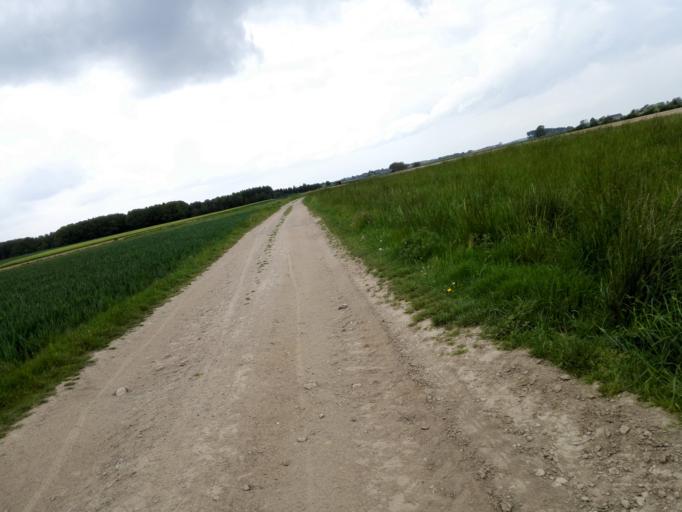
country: BE
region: Flanders
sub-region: Provincie Vlaams-Brabant
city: Huldenberg
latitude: 50.7942
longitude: 4.5711
